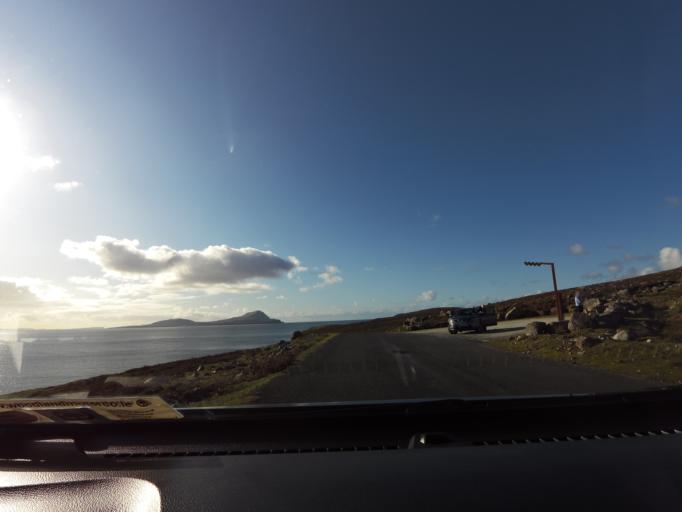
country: IE
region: Connaught
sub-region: Maigh Eo
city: Westport
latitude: 53.8670
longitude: -9.8681
